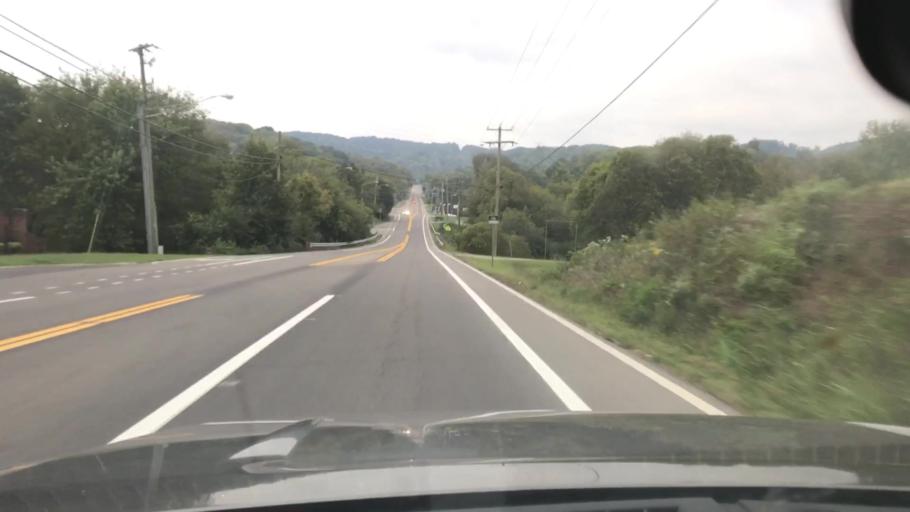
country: US
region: Tennessee
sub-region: Davidson County
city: Belle Meade
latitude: 36.1193
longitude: -86.9194
